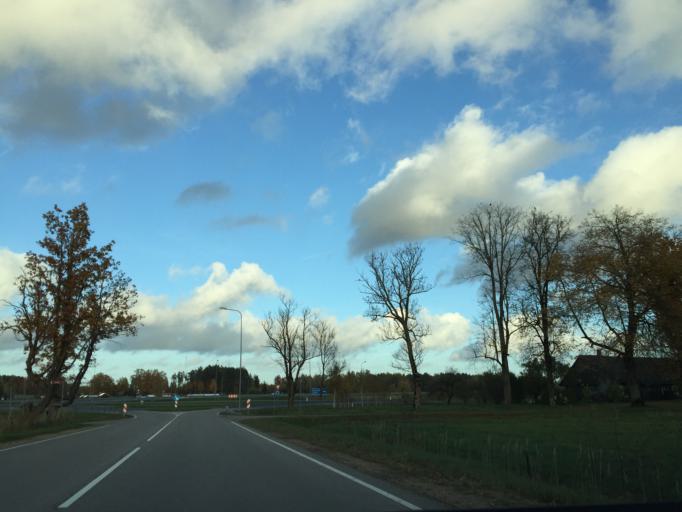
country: LV
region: Ogre
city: Jumprava
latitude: 56.7816
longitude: 25.0112
